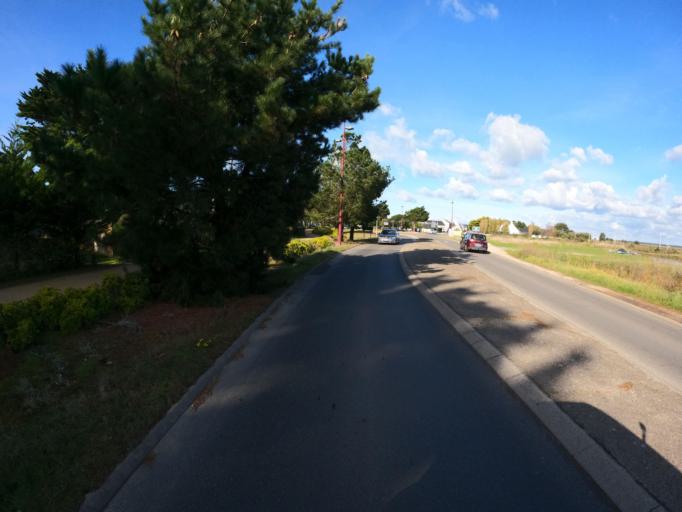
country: FR
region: Pays de la Loire
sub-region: Departement de la Loire-Atlantique
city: Le Croisic
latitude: 47.2824
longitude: -2.5023
